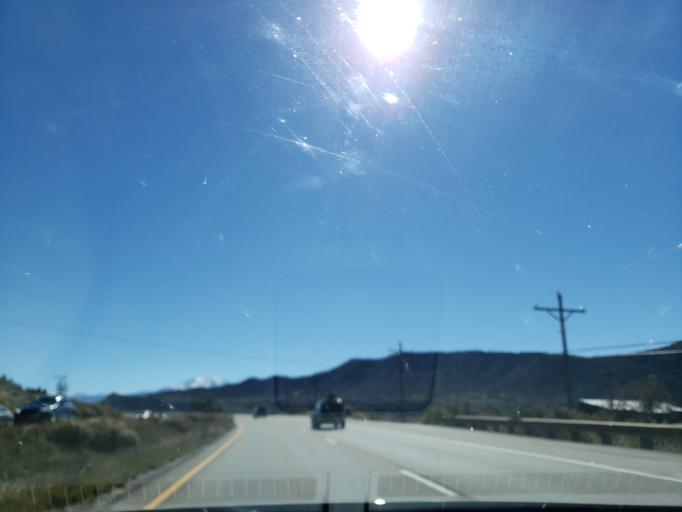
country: US
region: Colorado
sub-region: Garfield County
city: Glenwood Springs
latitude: 39.4894
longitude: -107.2982
